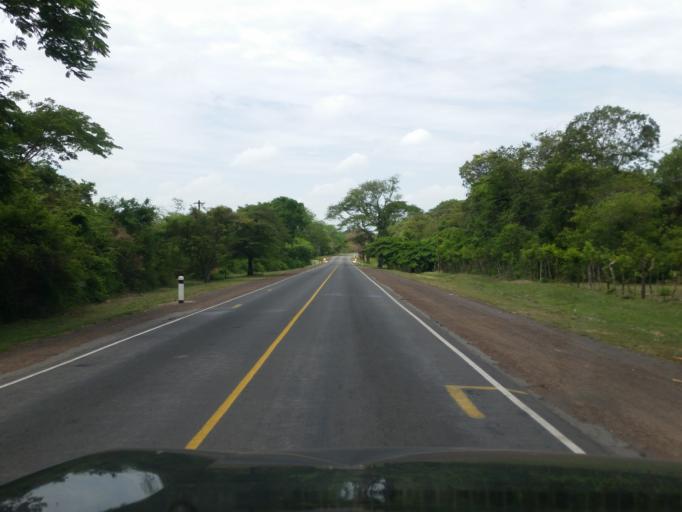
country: NI
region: Granada
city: Nandaime
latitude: 11.8071
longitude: -86.0442
